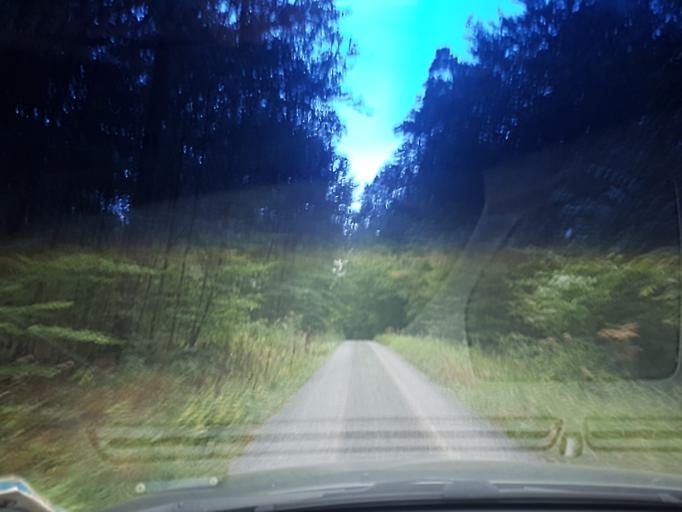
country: DE
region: Bavaria
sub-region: Upper Franconia
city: Burgwindheim
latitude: 49.8608
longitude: 10.5151
